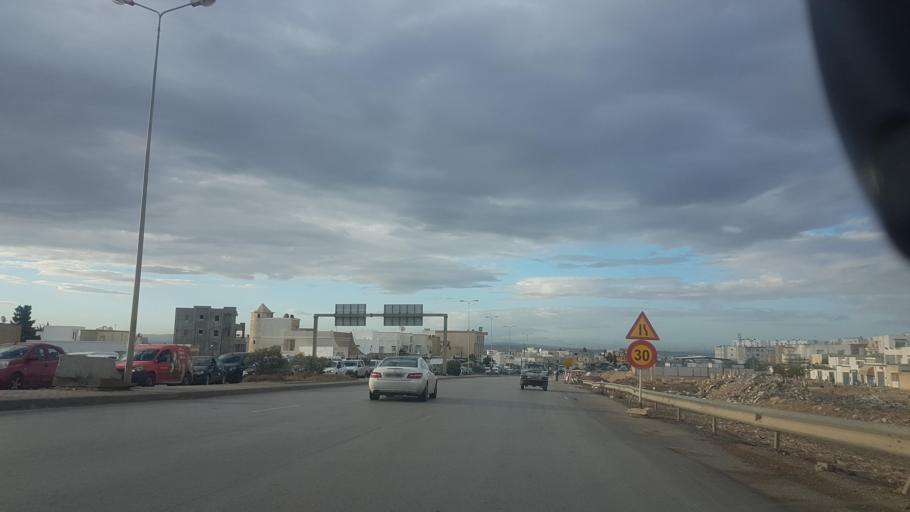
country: TN
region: Bin 'Arus
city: Ben Arous
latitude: 36.7442
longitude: 10.2080
